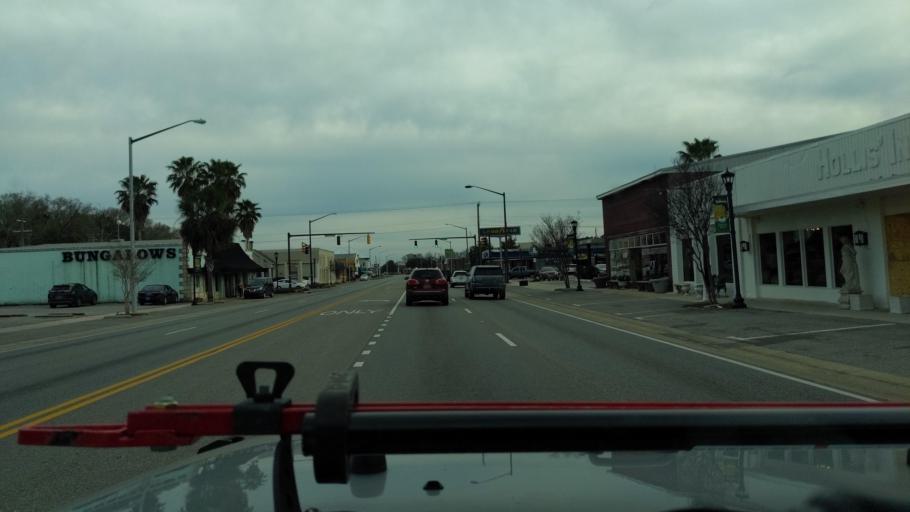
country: US
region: Alabama
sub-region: Baldwin County
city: Foley
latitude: 30.4051
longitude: -87.6838
